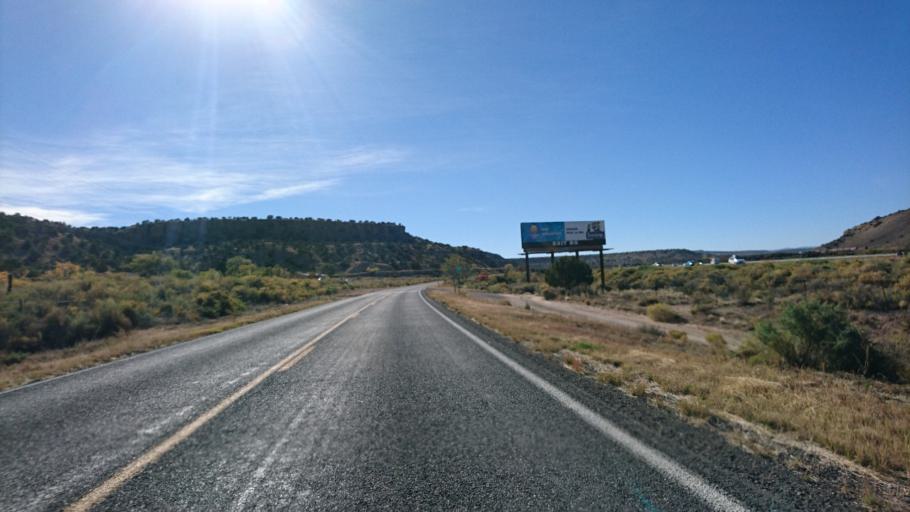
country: US
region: New Mexico
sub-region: Cibola County
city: Skyline-Ganipa
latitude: 35.0621
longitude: -107.6931
